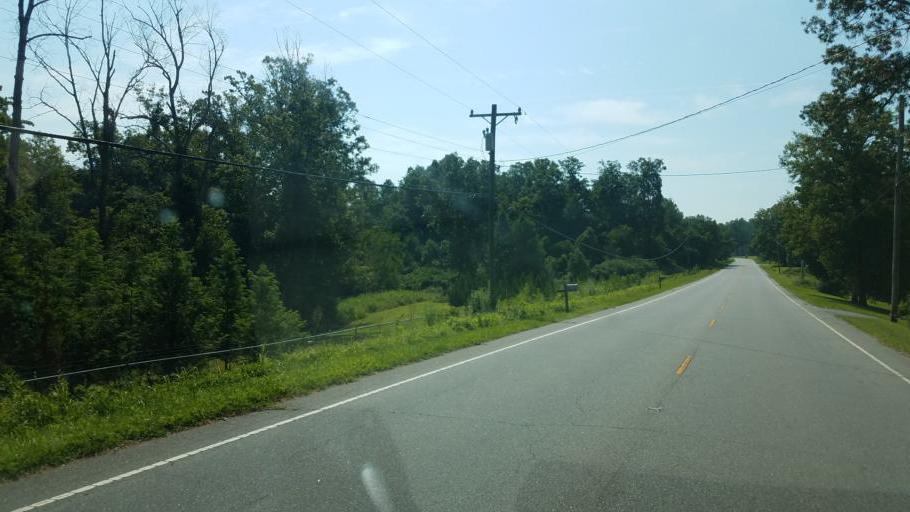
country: US
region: North Carolina
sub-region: Burke County
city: Glen Alpine
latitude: 35.7989
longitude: -81.7711
